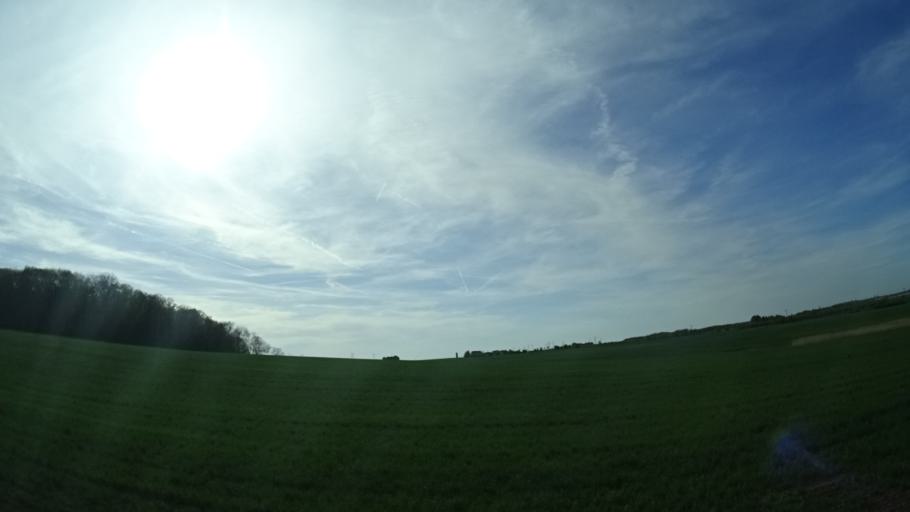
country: DE
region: Bavaria
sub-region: Regierungsbezirk Unterfranken
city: Kolitzheim
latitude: 49.9026
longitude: 10.2325
